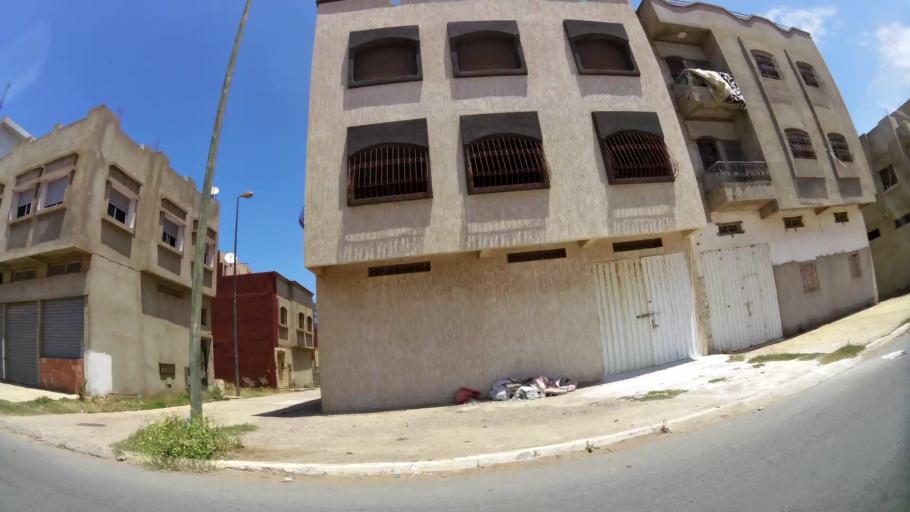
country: MA
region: Gharb-Chrarda-Beni Hssen
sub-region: Kenitra Province
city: Kenitra
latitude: 34.2497
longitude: -6.6256
